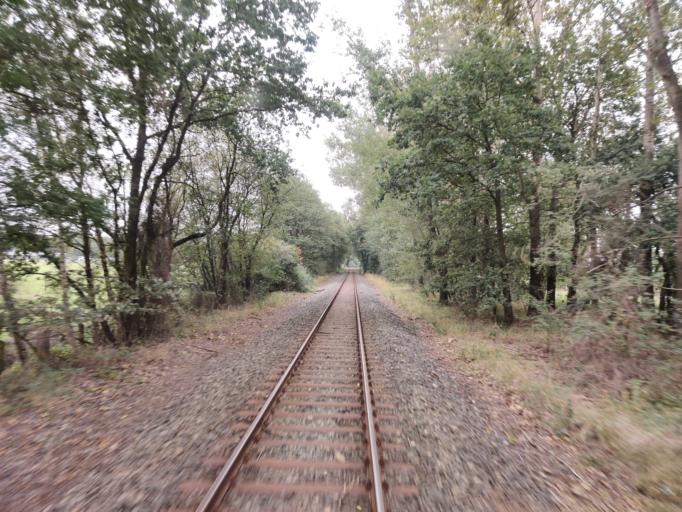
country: DE
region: Lower Saxony
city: Deinste
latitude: 53.5153
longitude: 9.3844
